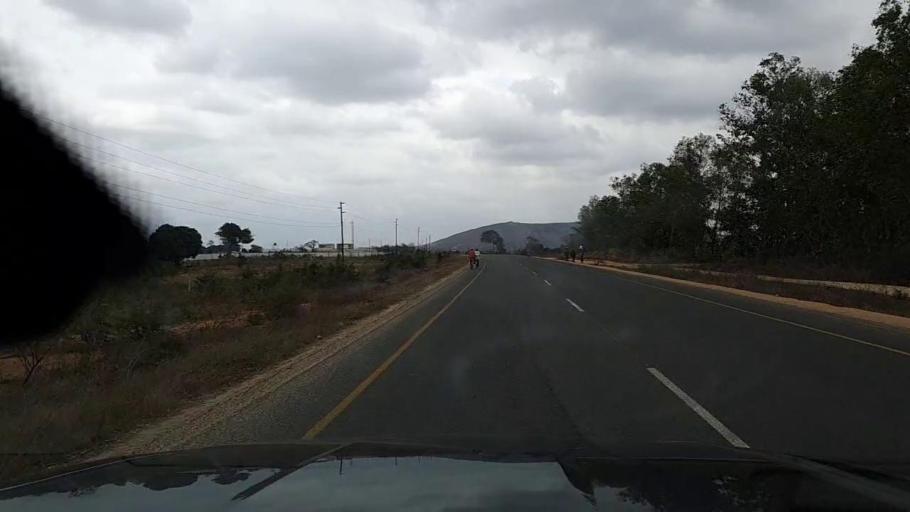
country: MZ
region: Nampula
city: Nampula
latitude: -15.1632
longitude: 39.3070
